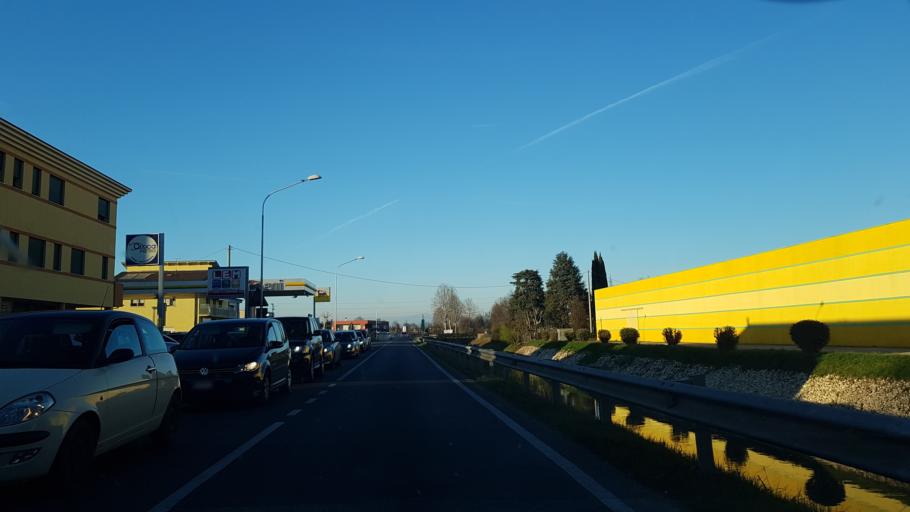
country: IT
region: Veneto
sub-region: Provincia di Vicenza
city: Ponte di Nanto
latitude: 45.4247
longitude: 11.5943
